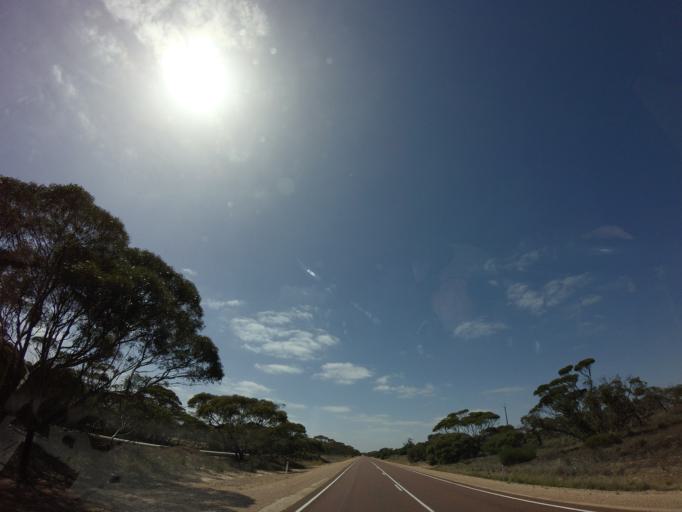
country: AU
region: South Australia
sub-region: Kimba
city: Caralue
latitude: -33.0998
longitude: 135.5206
